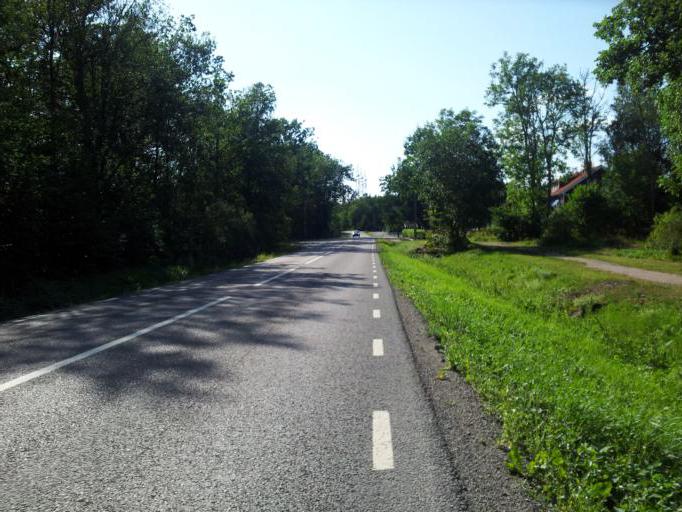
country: SE
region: Stockholm
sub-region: Norrtalje Kommun
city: Nykvarn
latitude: 59.8776
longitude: 18.0280
